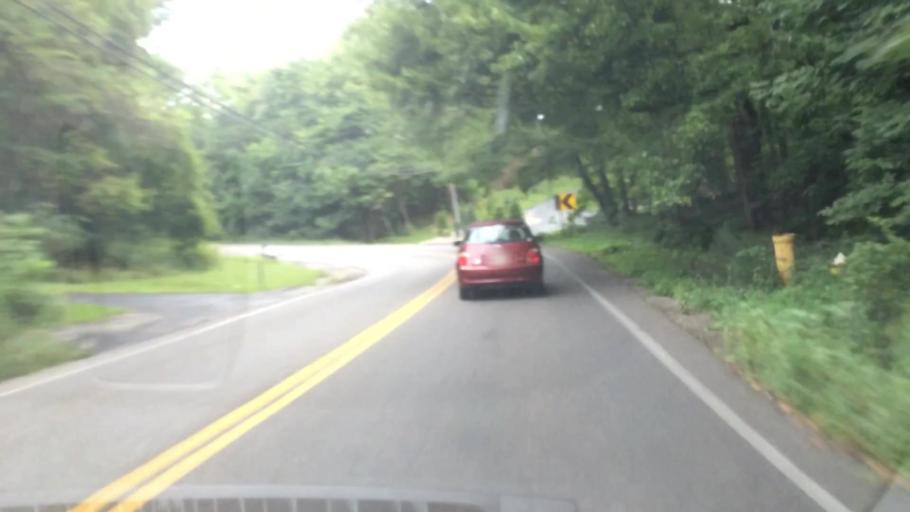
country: US
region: Ohio
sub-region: Summit County
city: Cuyahoga Falls
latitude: 41.1314
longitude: -81.5275
